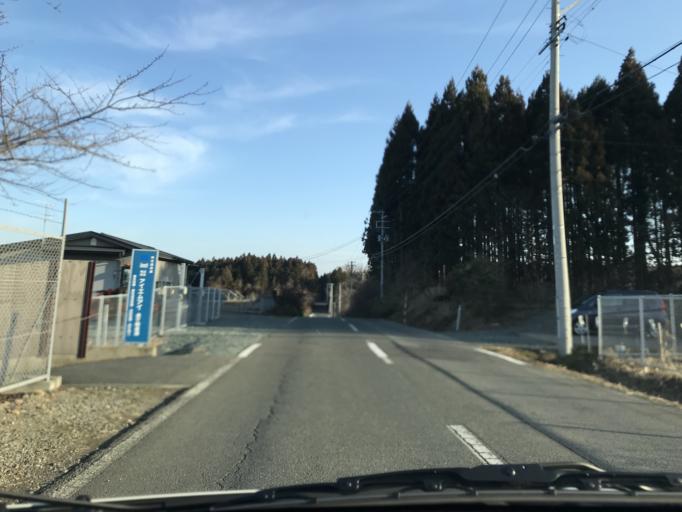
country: JP
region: Iwate
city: Kitakami
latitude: 39.2243
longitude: 141.1029
